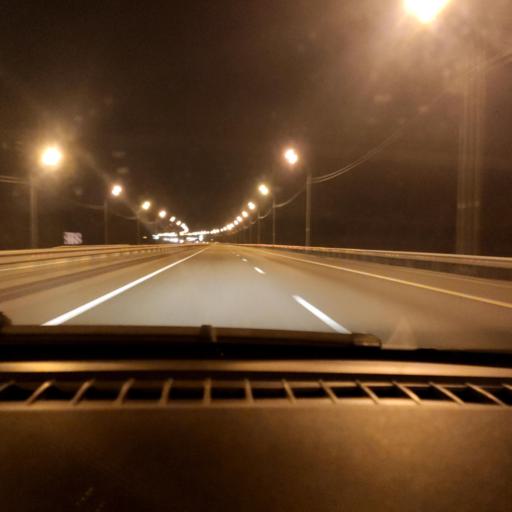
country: RU
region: Lipetsk
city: Khlevnoye
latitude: 52.2706
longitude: 39.0576
